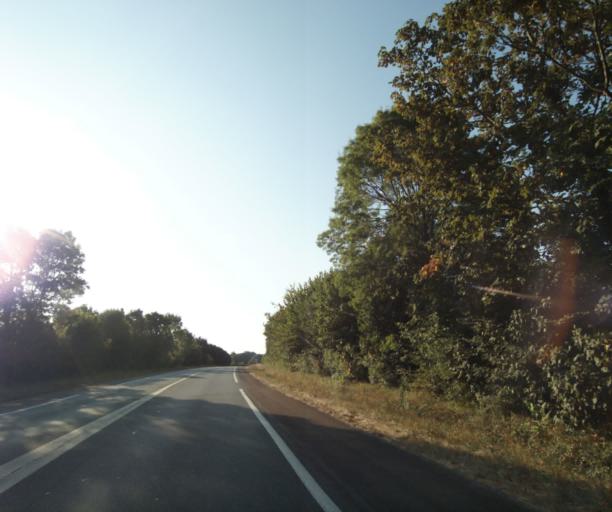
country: FR
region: Poitou-Charentes
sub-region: Departement de la Charente-Maritime
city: Tonnay-Charente
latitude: 45.9506
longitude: -0.8696
